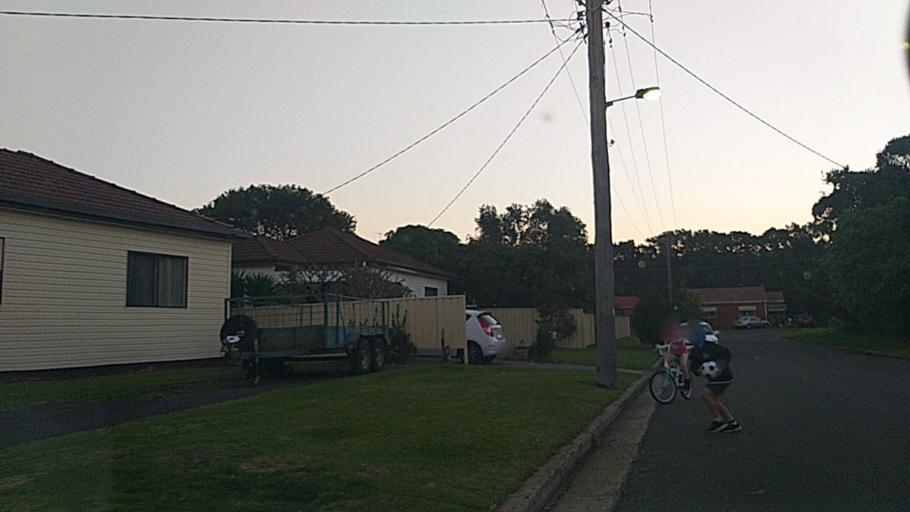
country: AU
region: New South Wales
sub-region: Wollongong
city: Corrimal
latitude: -34.3818
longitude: 150.9021
